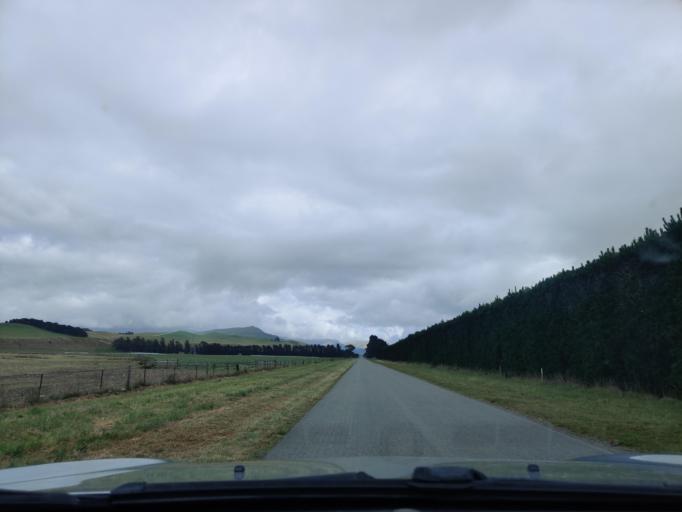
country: NZ
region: Canterbury
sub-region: Hurunui District
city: Amberley
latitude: -43.0749
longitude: 172.6835
